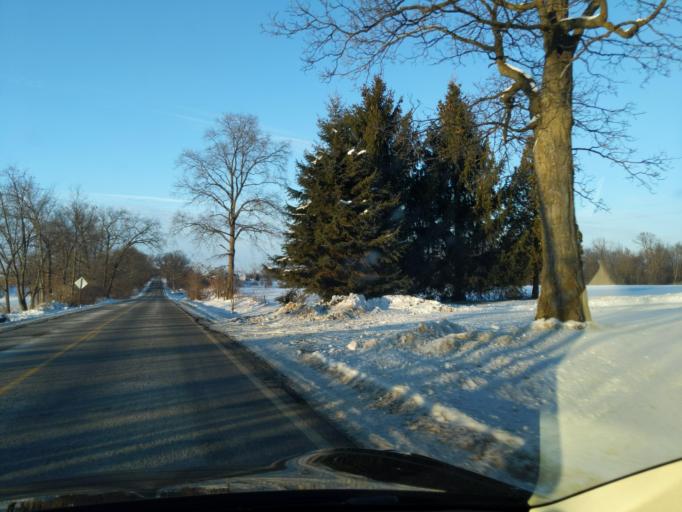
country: US
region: Michigan
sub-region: Livingston County
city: Fowlerville
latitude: 42.5582
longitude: -84.1130
